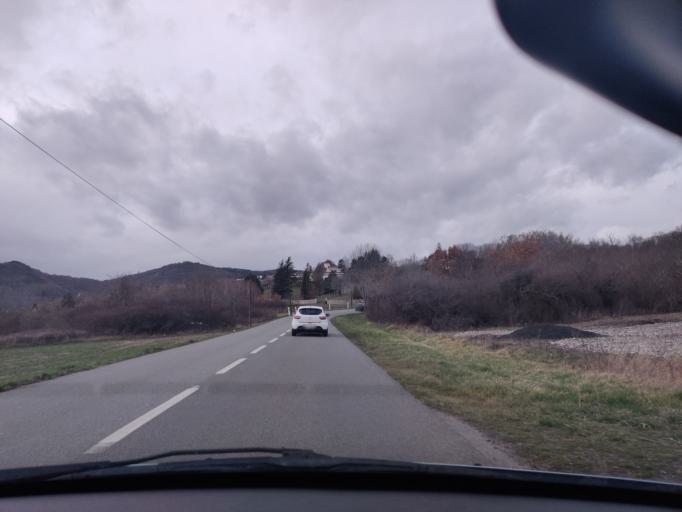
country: FR
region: Auvergne
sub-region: Departement du Puy-de-Dome
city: Chatel-Guyon
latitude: 45.8969
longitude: 3.0701
